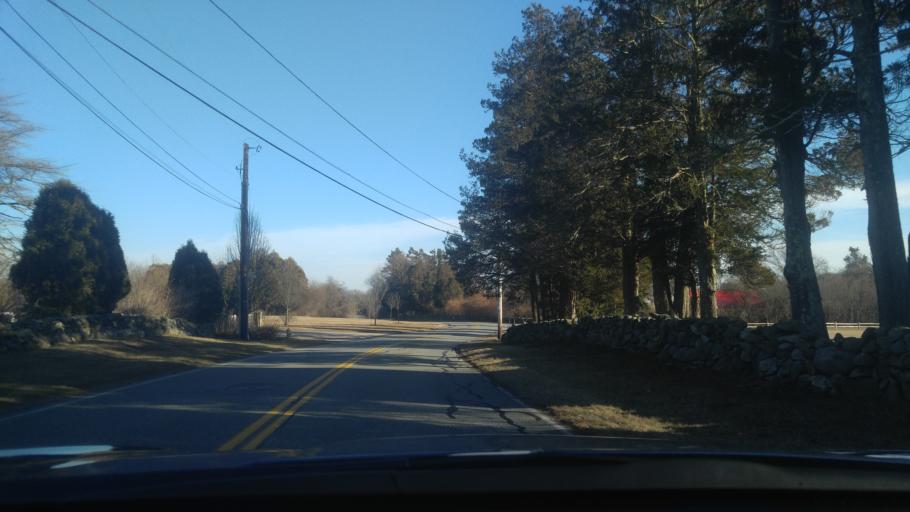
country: US
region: Rhode Island
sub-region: Washington County
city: Narragansett Pier
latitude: 41.4000
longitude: -71.4764
